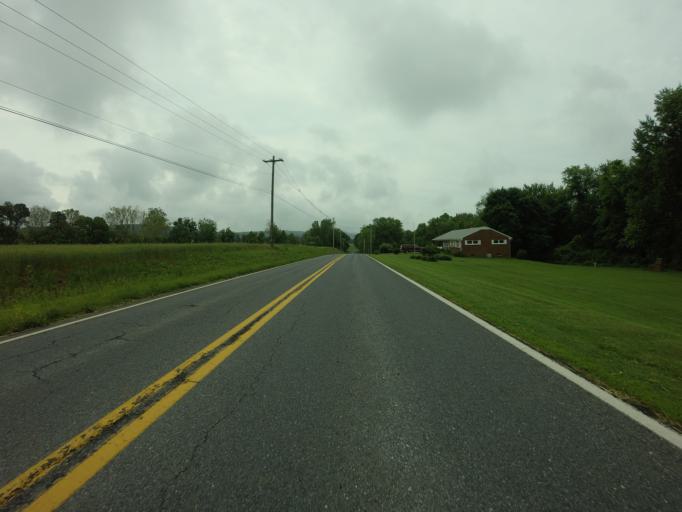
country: US
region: Maryland
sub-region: Frederick County
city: Jefferson
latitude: 39.3572
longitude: -77.5319
